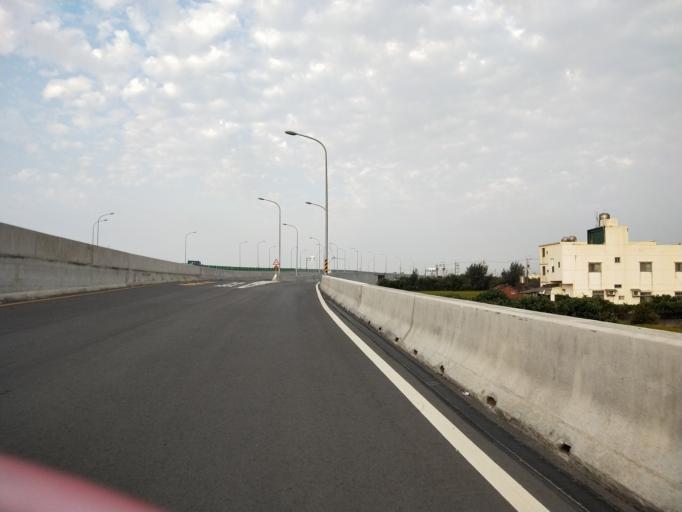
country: TW
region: Taiwan
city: Fengyuan
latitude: 24.3872
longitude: 120.5948
